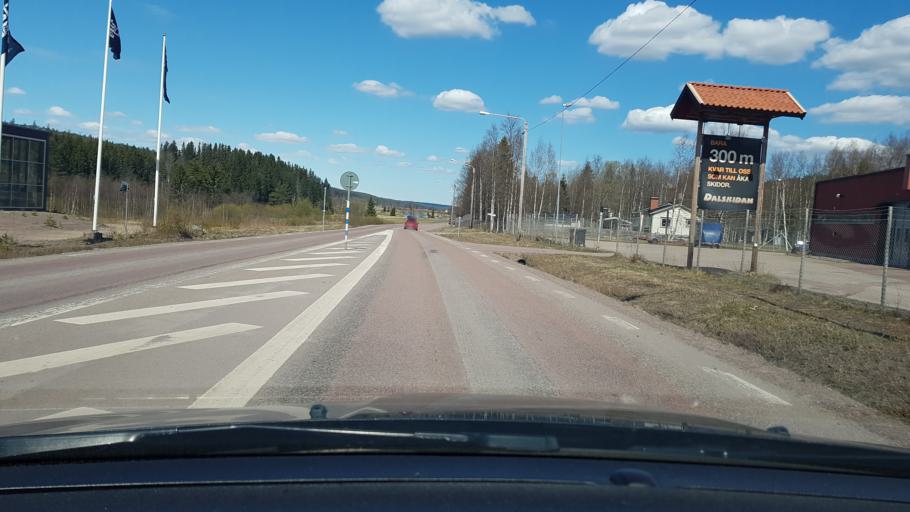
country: SE
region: Dalarna
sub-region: Malung-Saelens kommun
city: Malung
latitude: 61.1359
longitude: 13.2816
